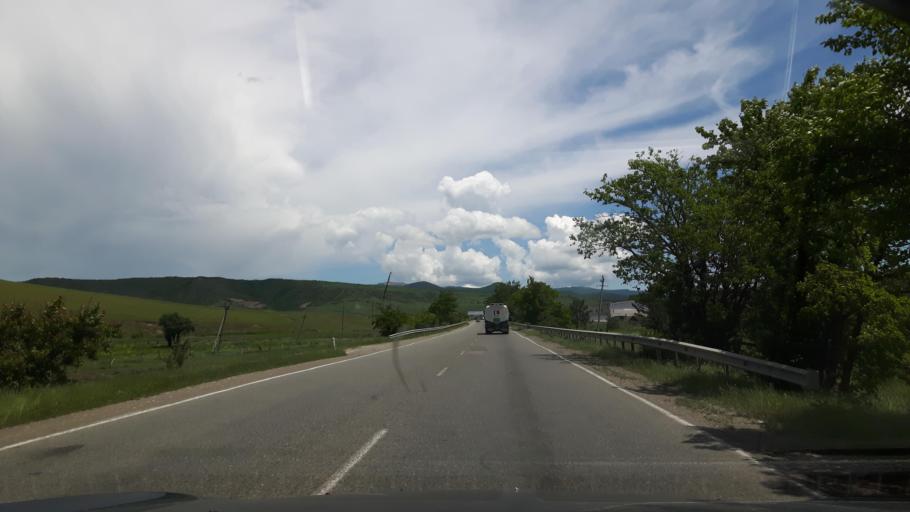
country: GE
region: Kakheti
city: Sagarejo
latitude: 41.7276
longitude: 45.1897
